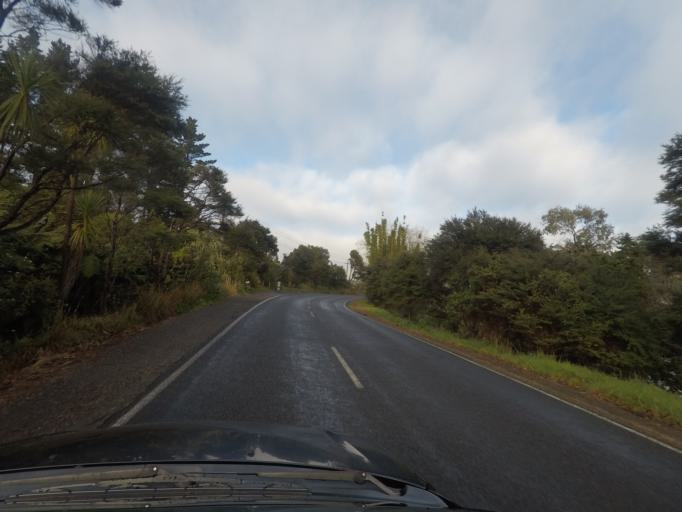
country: NZ
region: Auckland
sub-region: Auckland
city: Waitakere
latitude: -36.9111
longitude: 174.6083
